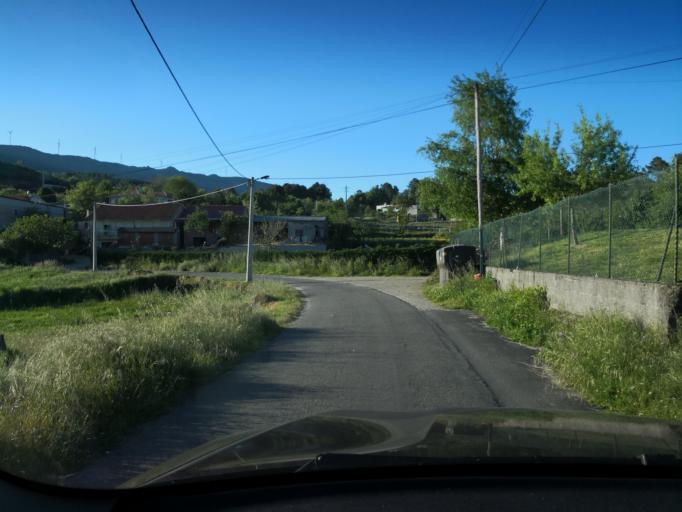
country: PT
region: Vila Real
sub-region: Vila Real
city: Vila Real
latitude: 41.3487
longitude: -7.7263
